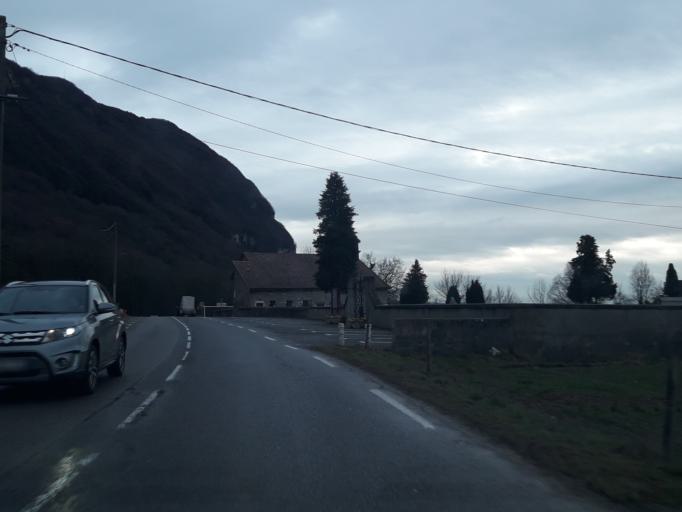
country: FR
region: Rhone-Alpes
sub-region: Departement de la Haute-Savoie
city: Etrembieres
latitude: 46.1777
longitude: 6.2285
